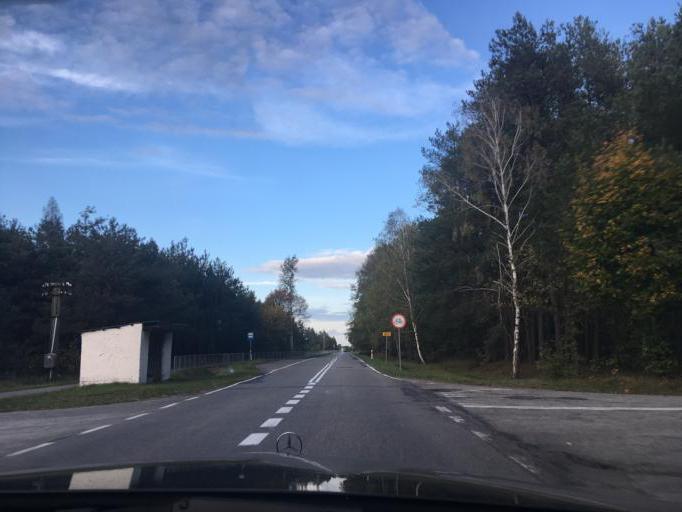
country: PL
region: Lublin Voivodeship
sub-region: Powiat bialski
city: Slawatycze
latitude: 51.7384
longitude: 23.5248
